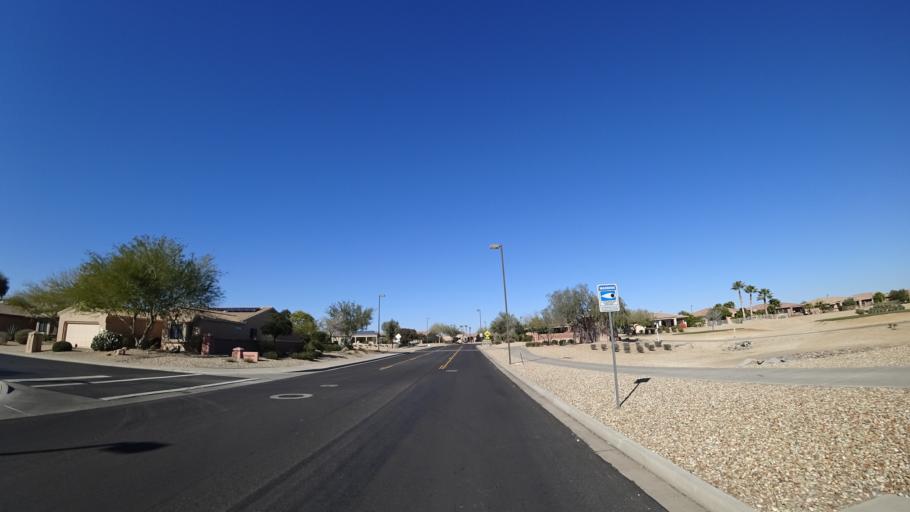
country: US
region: Arizona
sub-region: Maricopa County
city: Sun City West
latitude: 33.6543
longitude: -112.4268
